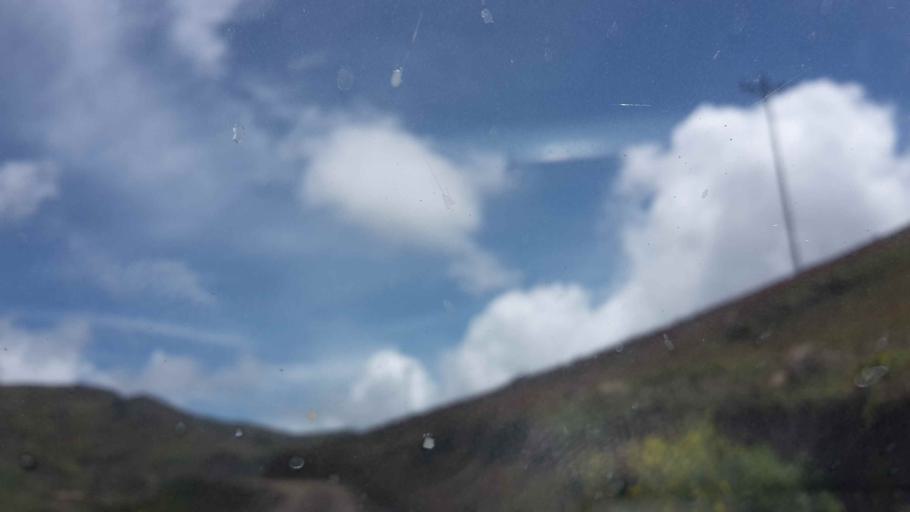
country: BO
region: Cochabamba
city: Cochabamba
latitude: -17.1922
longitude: -66.0798
